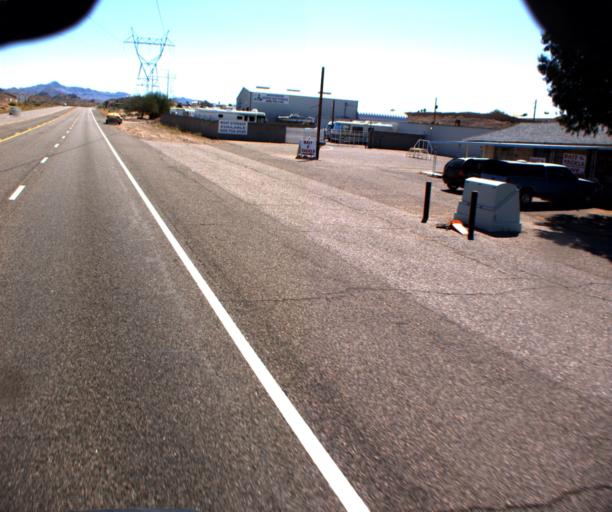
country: US
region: Nevada
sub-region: Clark County
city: Laughlin
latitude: 35.1900
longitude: -114.5344
